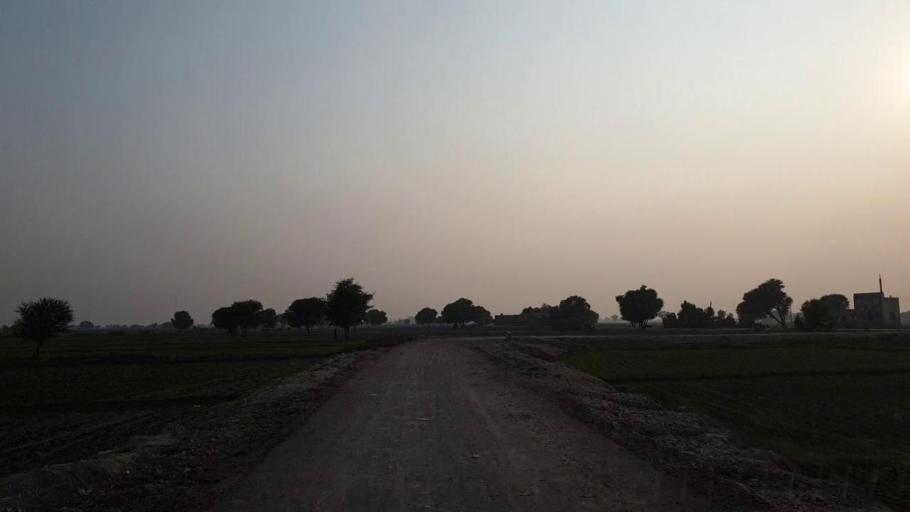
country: PK
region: Sindh
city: Bhan
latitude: 26.4948
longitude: 67.7390
